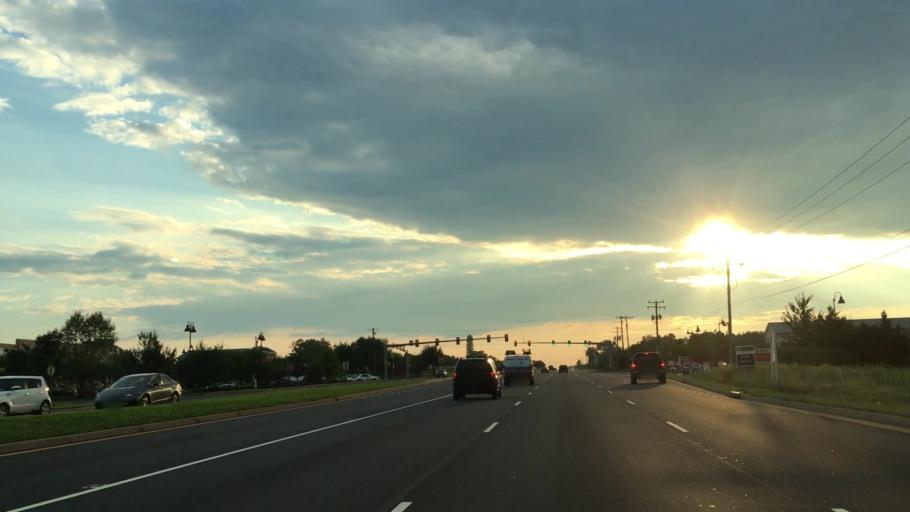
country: US
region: Virginia
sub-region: Spotsylvania County
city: Spotsylvania
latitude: 38.2913
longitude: -77.5659
